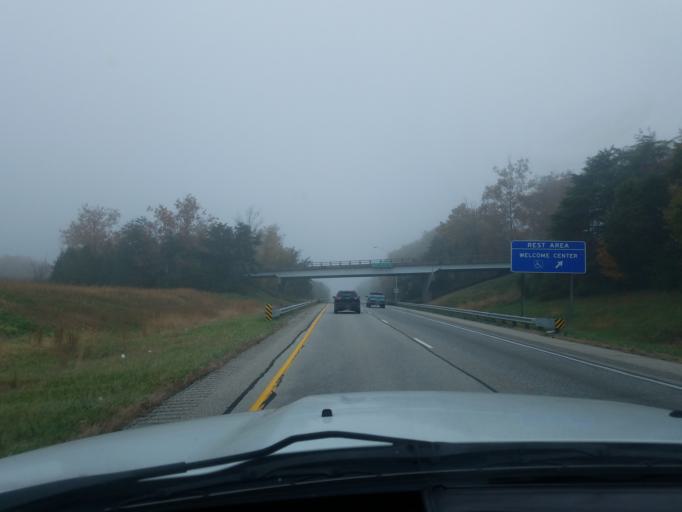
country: US
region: Indiana
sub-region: Floyd County
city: Georgetown
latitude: 38.2783
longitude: -85.9542
